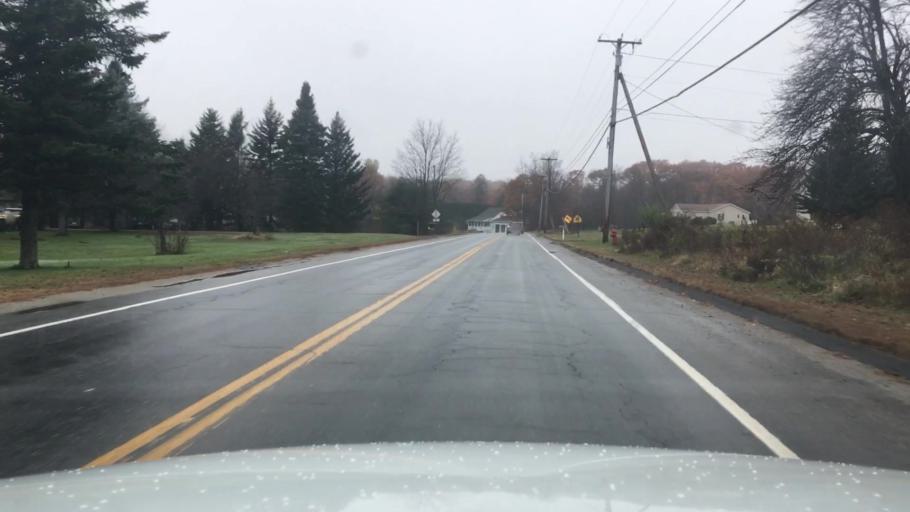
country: US
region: Maine
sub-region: Androscoggin County
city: Sabattus
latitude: 44.1112
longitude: -70.0910
